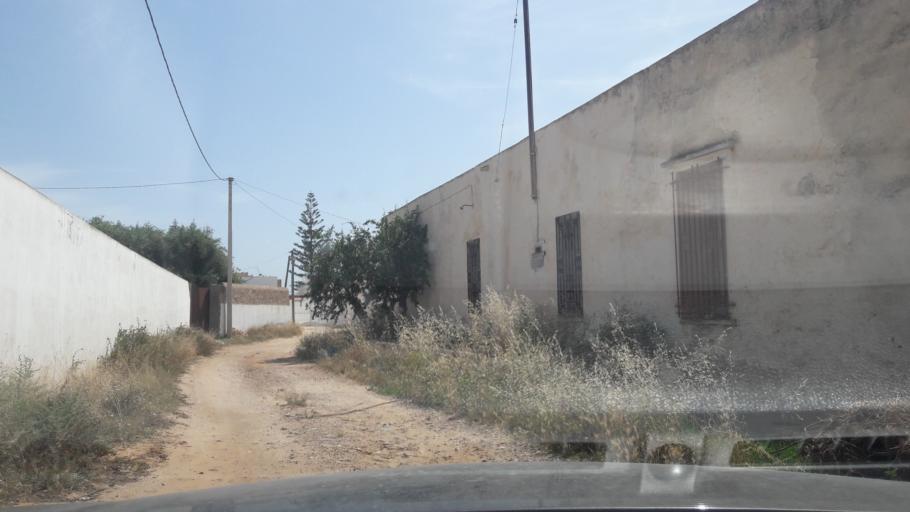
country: TN
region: Safaqis
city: Sfax
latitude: 34.7903
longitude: 10.7534
